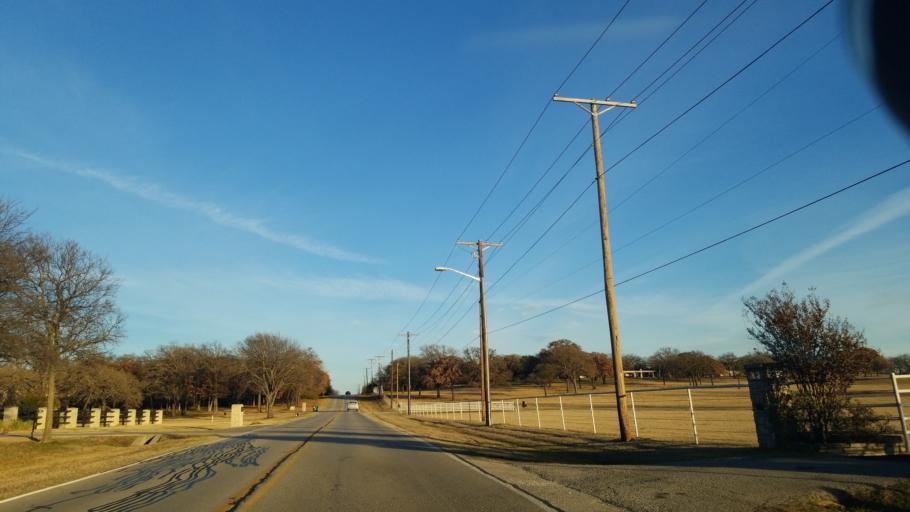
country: US
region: Texas
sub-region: Denton County
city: Denton
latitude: 33.1760
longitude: -97.1376
